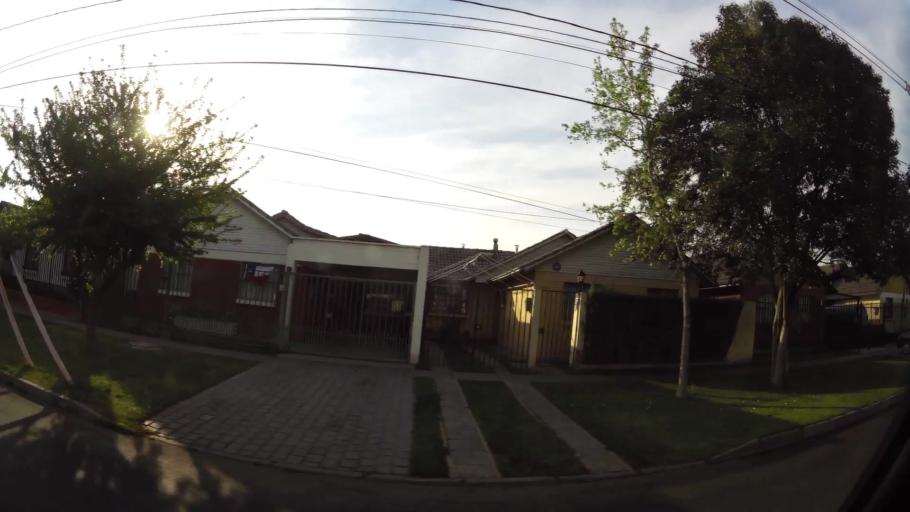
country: CL
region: Santiago Metropolitan
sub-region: Provincia de Maipo
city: San Bernardo
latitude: -33.5605
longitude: -70.7853
